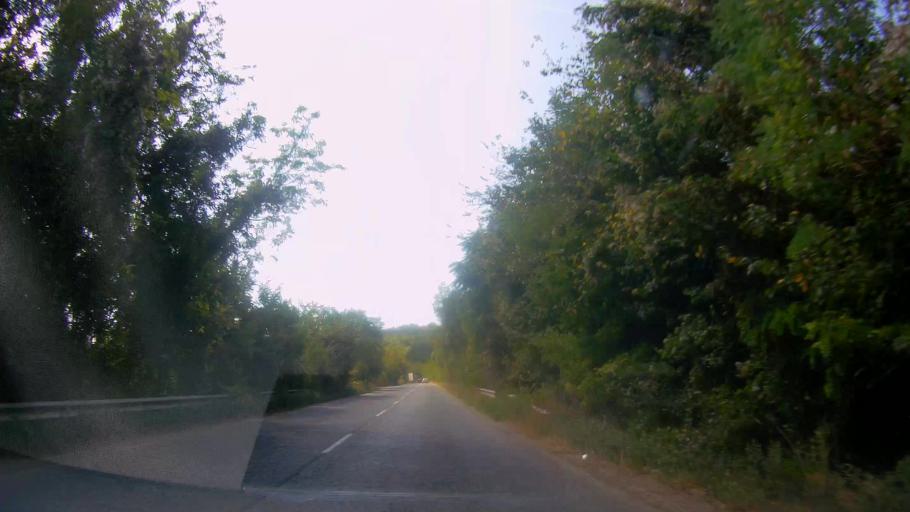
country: BG
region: Veliko Turnovo
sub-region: Obshtina Polski Trumbesh
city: Polski Trumbesh
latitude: 43.4413
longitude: 25.6550
